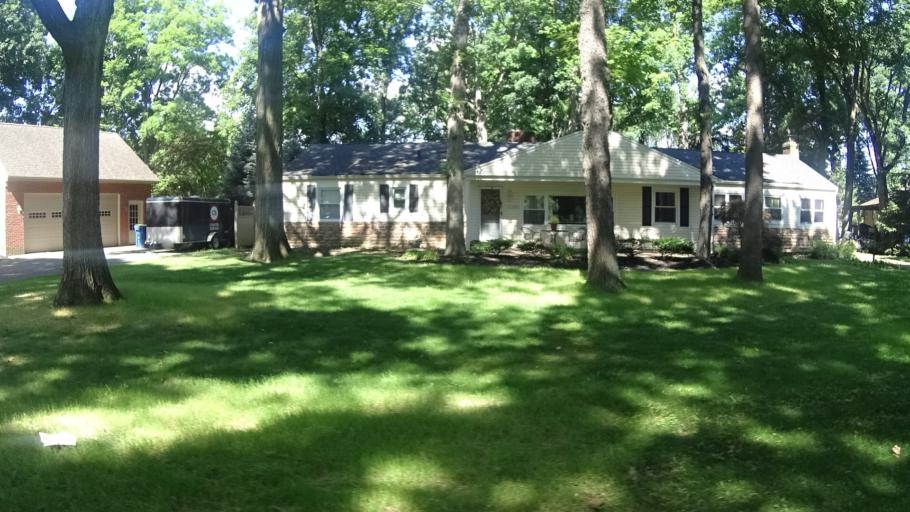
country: US
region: Ohio
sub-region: Erie County
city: Sandusky
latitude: 41.4112
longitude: -82.6541
